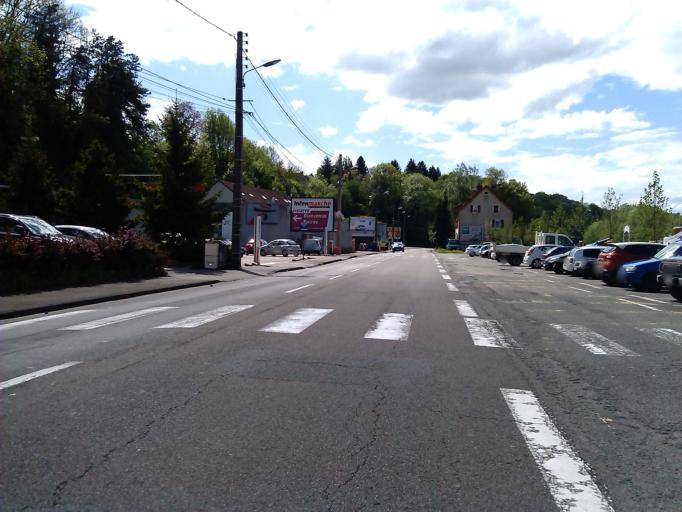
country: FR
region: Franche-Comte
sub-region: Departement du Doubs
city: Arbouans
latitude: 47.5040
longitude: 6.7931
